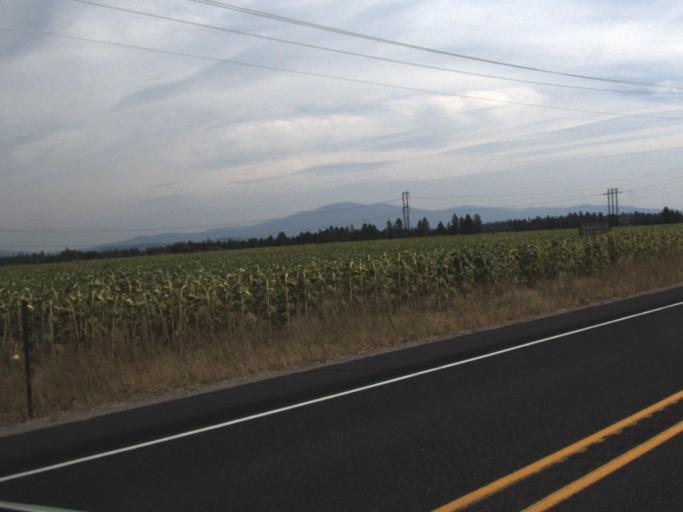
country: US
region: Washington
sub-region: Spokane County
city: Deer Park
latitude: 47.9634
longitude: -117.5012
